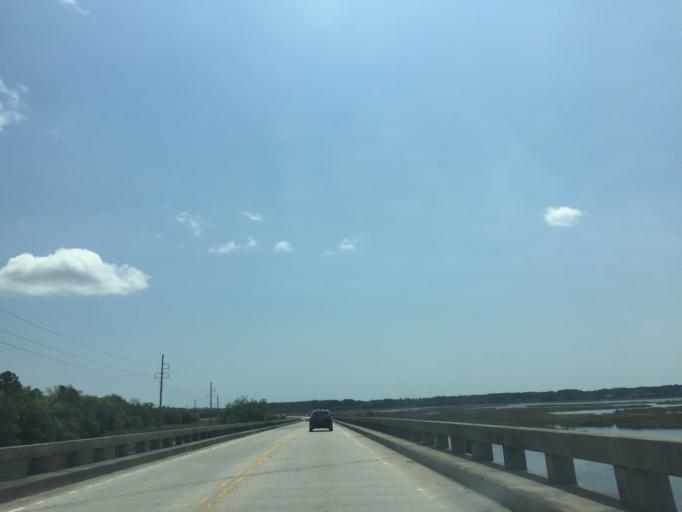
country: US
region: Georgia
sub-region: Chatham County
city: Isle of Hope
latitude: 31.9516
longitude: -81.0832
